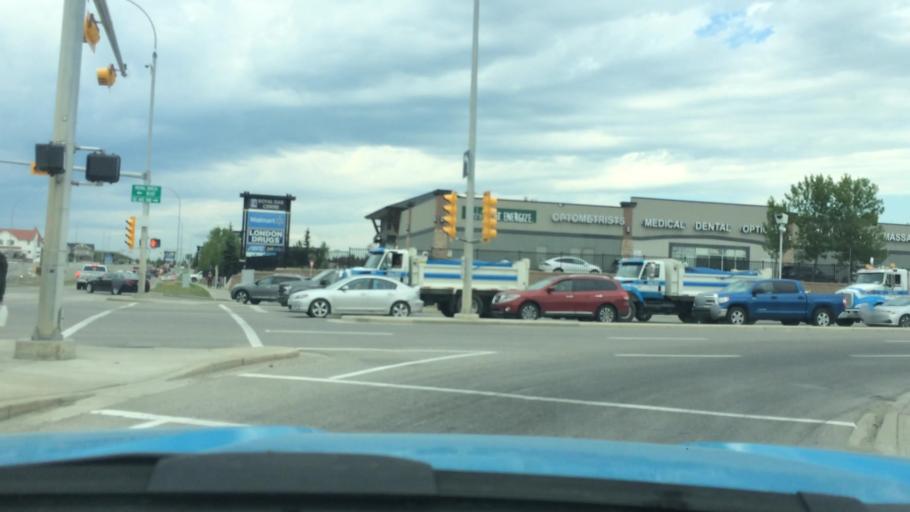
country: CA
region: Alberta
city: Calgary
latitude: 51.1498
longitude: -114.2130
